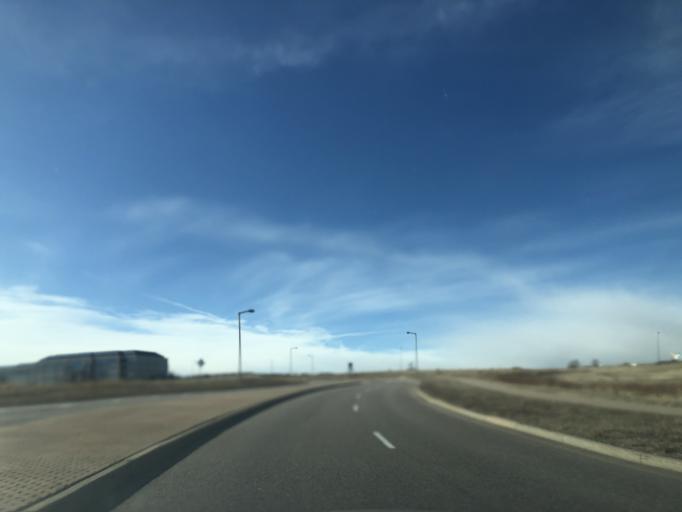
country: US
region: Colorado
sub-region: Douglas County
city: Meridian
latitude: 39.5531
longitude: -104.8631
